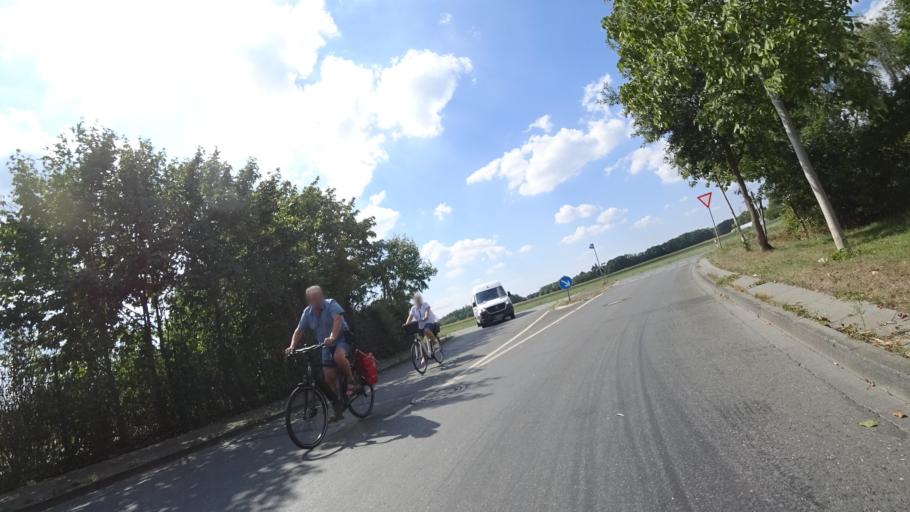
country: DE
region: North Rhine-Westphalia
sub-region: Regierungsbezirk Detmold
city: Rheda-Wiedenbruck
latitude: 51.8678
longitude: 8.2963
